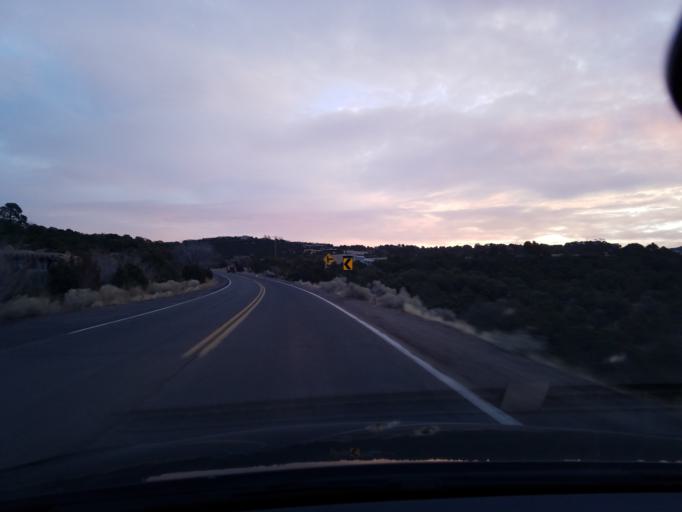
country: US
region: New Mexico
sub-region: Santa Fe County
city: Santa Fe
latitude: 35.6950
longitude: -105.9141
